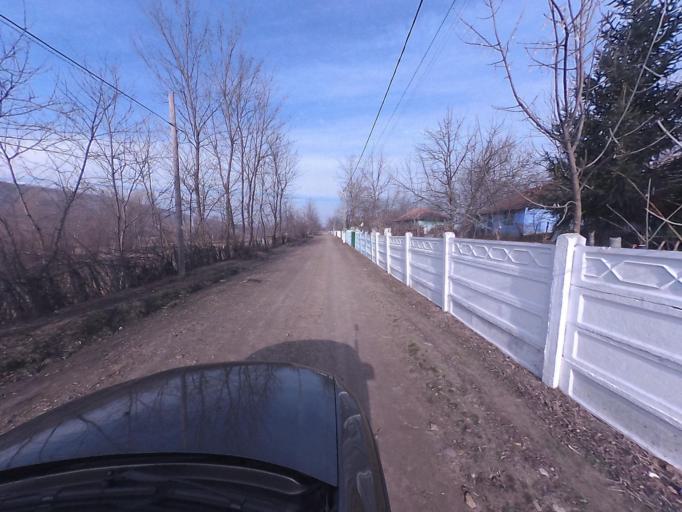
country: RO
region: Vaslui
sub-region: Comuna Solesti
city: Solesti
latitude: 46.8059
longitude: 27.7819
